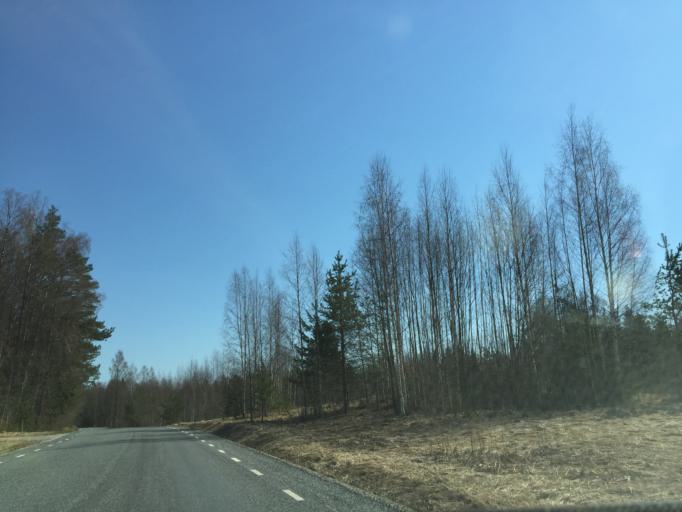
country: EE
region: Tartu
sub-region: Alatskivi vald
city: Kallaste
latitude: 58.5782
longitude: 27.0103
